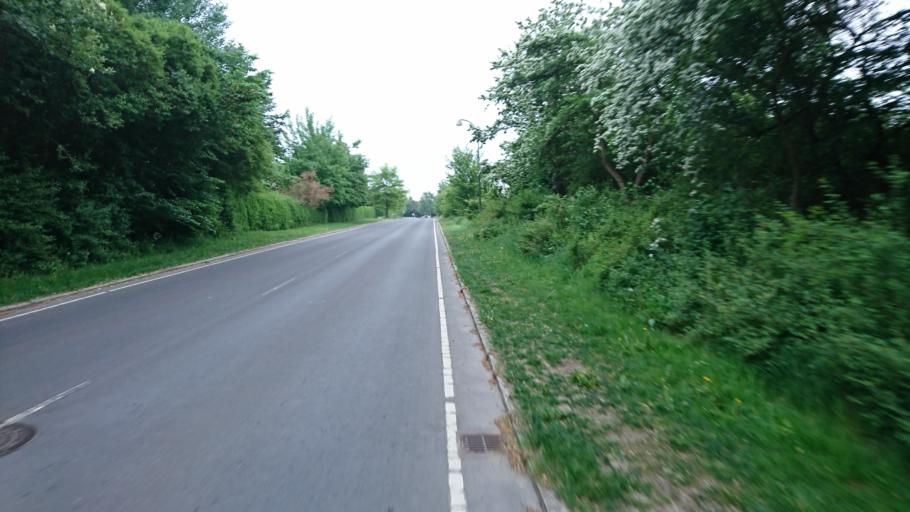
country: DK
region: Capital Region
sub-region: Herlev Kommune
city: Herlev
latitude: 55.7386
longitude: 12.4053
